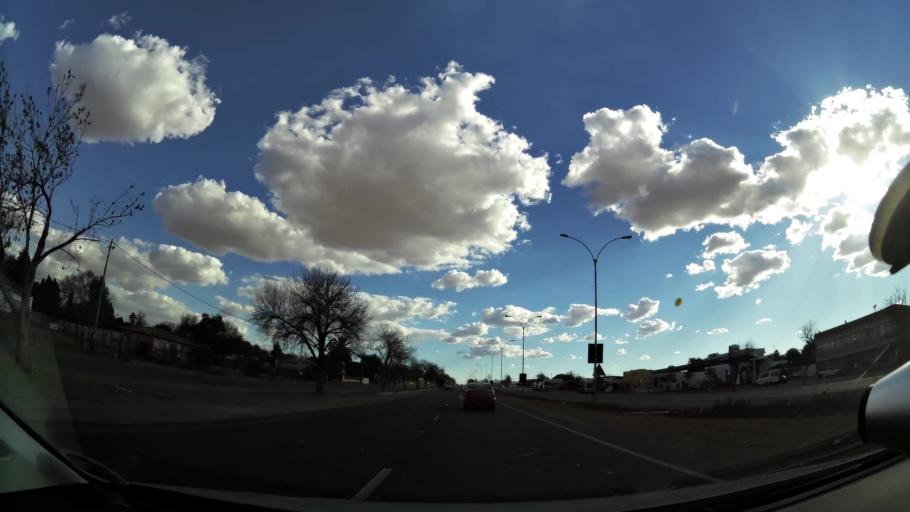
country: ZA
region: North-West
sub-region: Dr Kenneth Kaunda District Municipality
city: Klerksdorp
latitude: -26.8648
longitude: 26.6443
